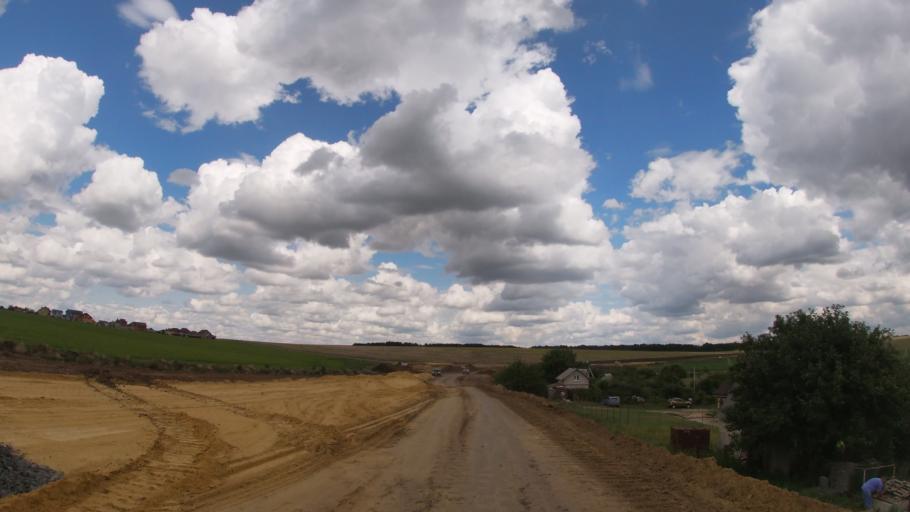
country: RU
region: Belgorod
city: Mayskiy
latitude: 50.5163
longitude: 36.4914
